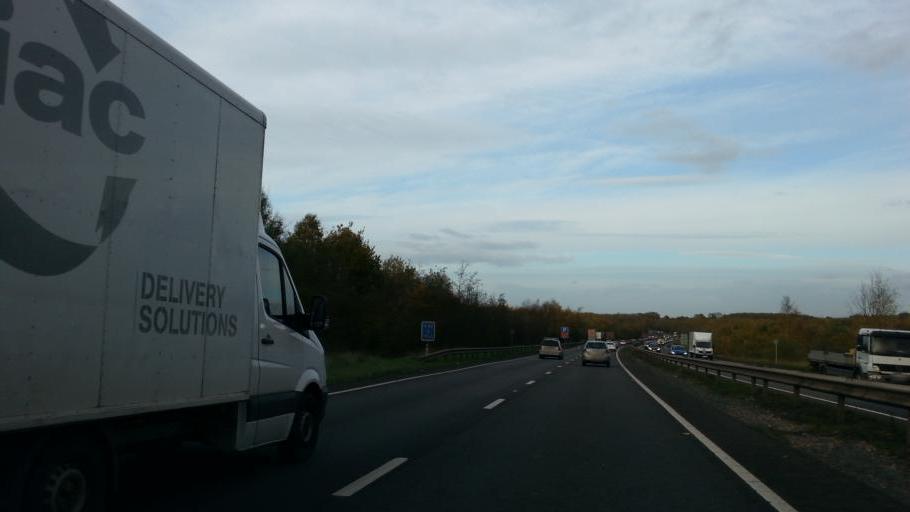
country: GB
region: England
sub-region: Leicestershire
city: Ashby de la Zouch
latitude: 52.7633
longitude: -1.4321
